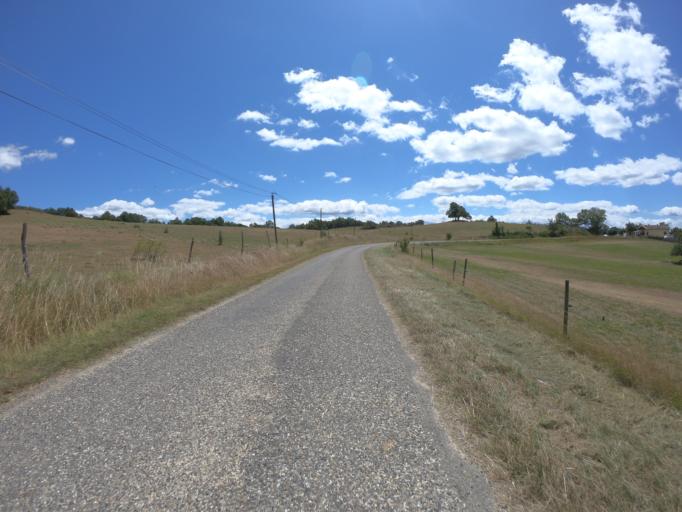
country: FR
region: Midi-Pyrenees
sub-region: Departement de l'Ariege
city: Mirepoix
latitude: 43.0510
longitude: 1.8364
